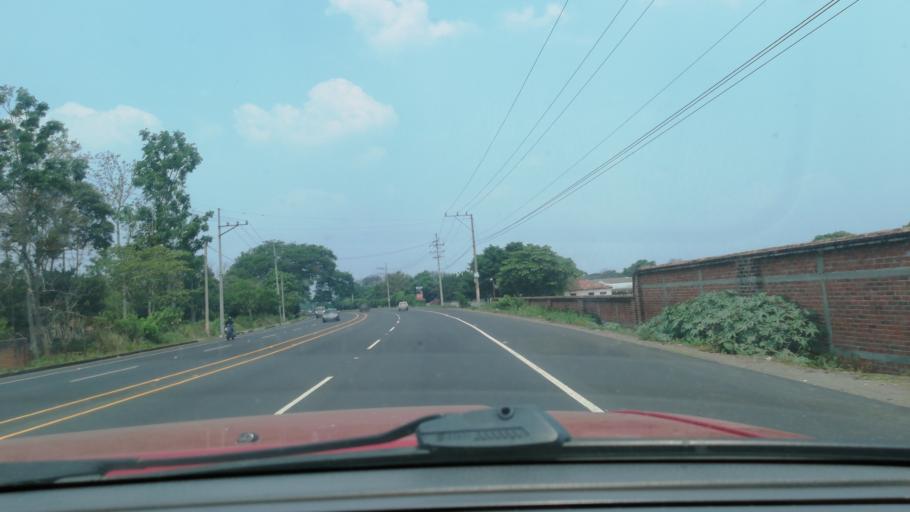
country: SV
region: Santa Ana
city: Santa Ana
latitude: 13.9887
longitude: -89.6198
